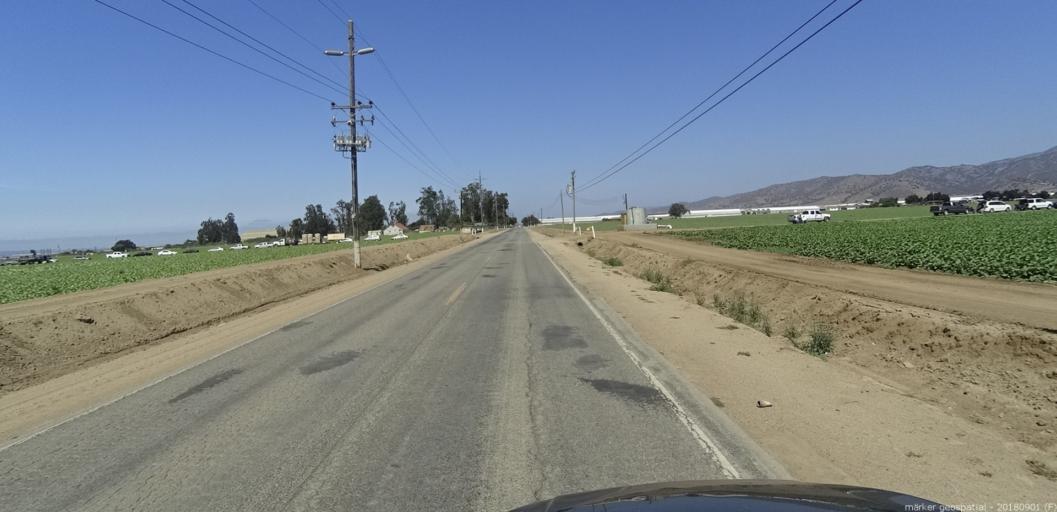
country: US
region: California
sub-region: Monterey County
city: Chualar
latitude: 36.6130
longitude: -121.5199
